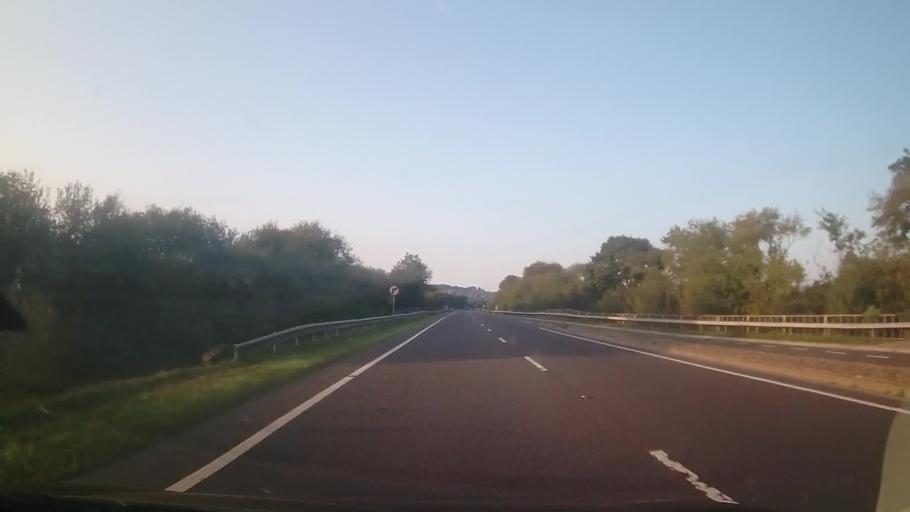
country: GB
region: Wales
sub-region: Sir Powys
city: Welshpool
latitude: 52.6455
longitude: -3.1441
